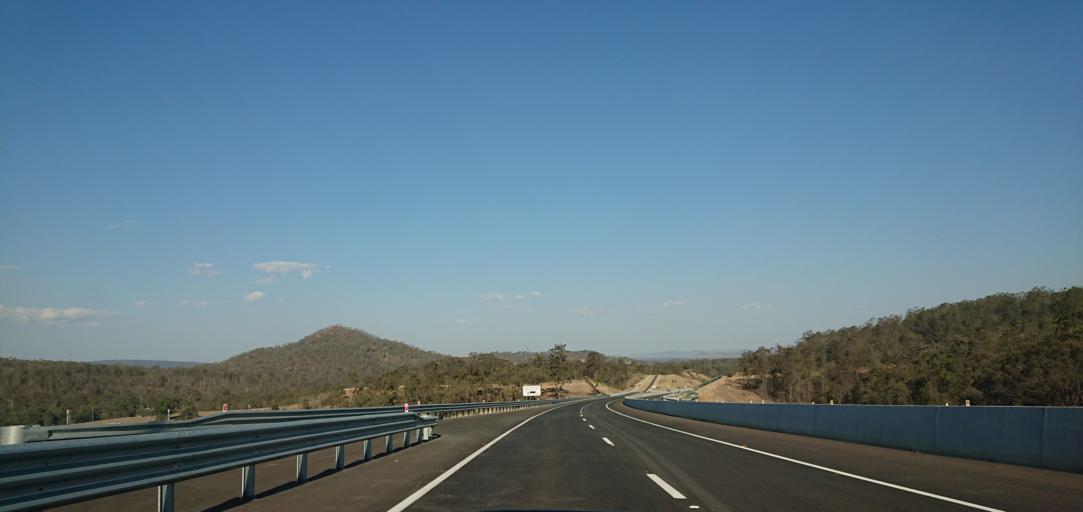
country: AU
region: Queensland
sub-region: Toowoomba
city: East Toowoomba
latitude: -27.5079
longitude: 152.0113
